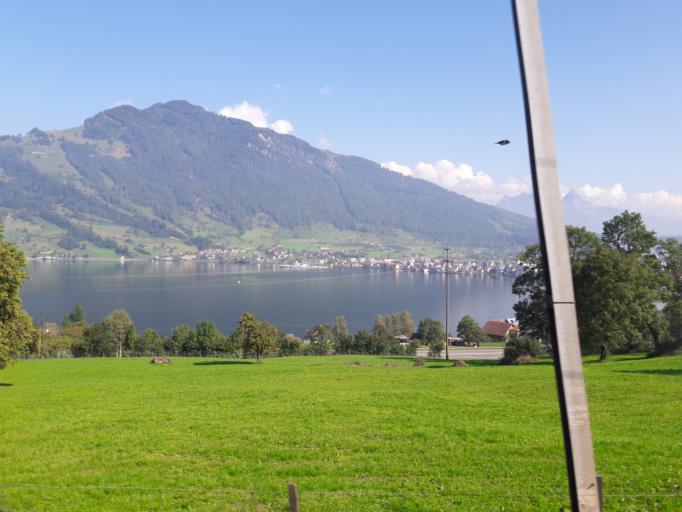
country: CH
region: Schwyz
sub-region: Bezirk Schwyz
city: Arth
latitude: 47.0659
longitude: 8.5060
